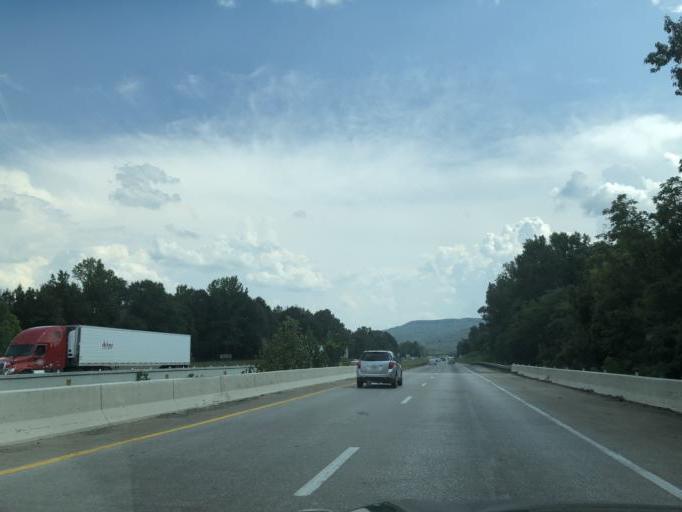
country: US
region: Tennessee
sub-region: Marion County
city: Monteagle
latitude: 35.2871
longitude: -85.8948
